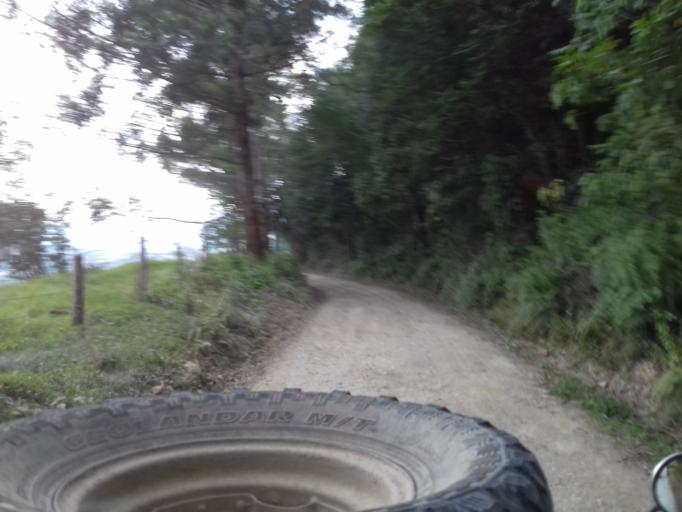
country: CO
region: Quindio
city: Salento
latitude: 4.6294
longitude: -75.5576
